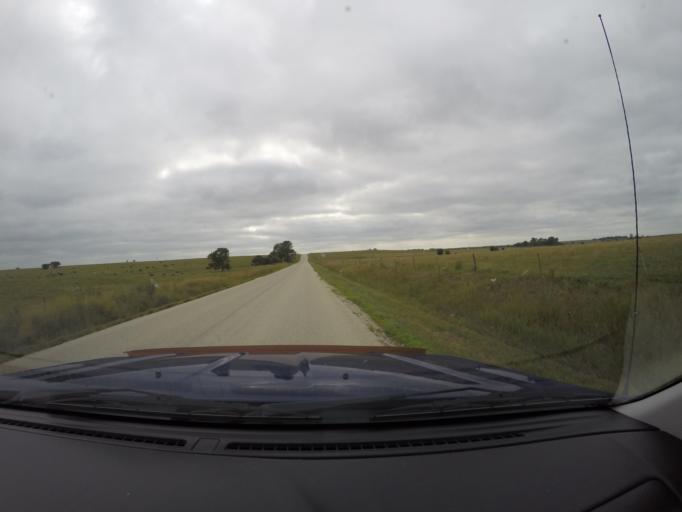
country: US
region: Kansas
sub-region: Dickinson County
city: Herington
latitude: 38.7975
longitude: -96.7632
